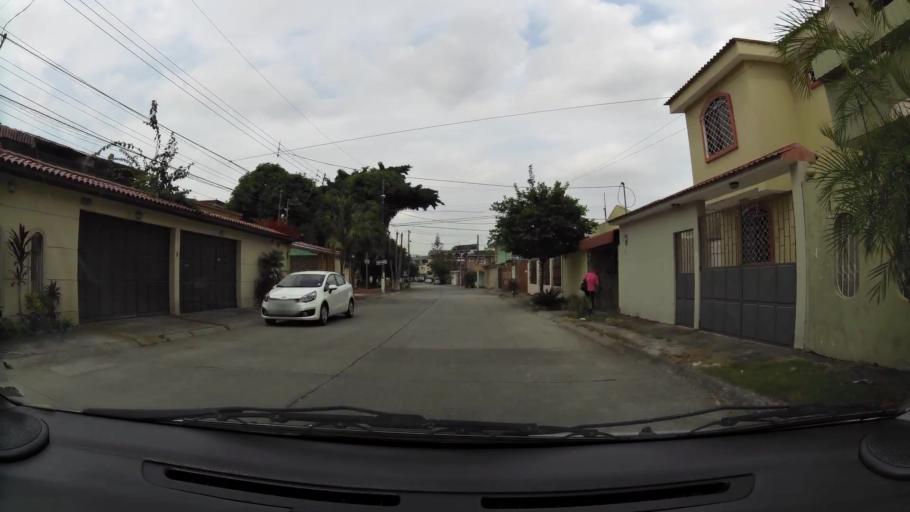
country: EC
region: Guayas
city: Eloy Alfaro
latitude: -2.1152
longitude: -79.8945
